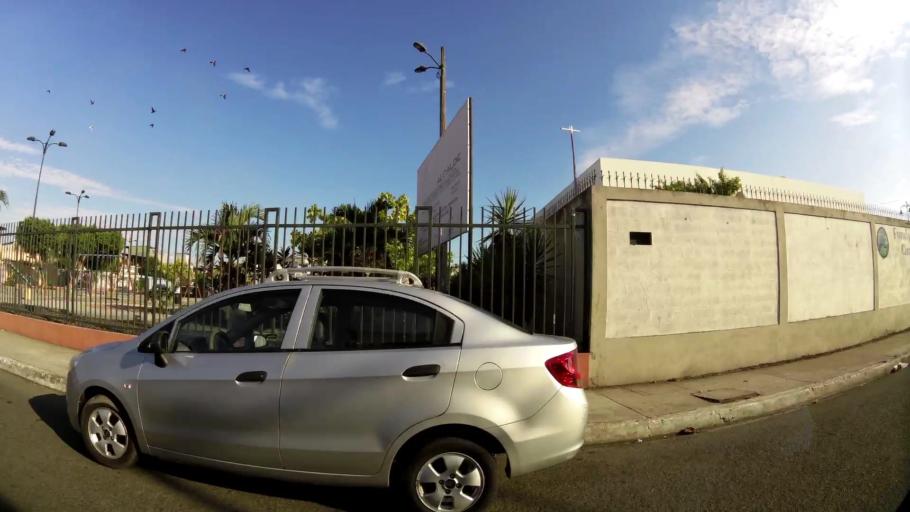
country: EC
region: Guayas
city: Guayaquil
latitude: -2.2249
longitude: -79.9067
